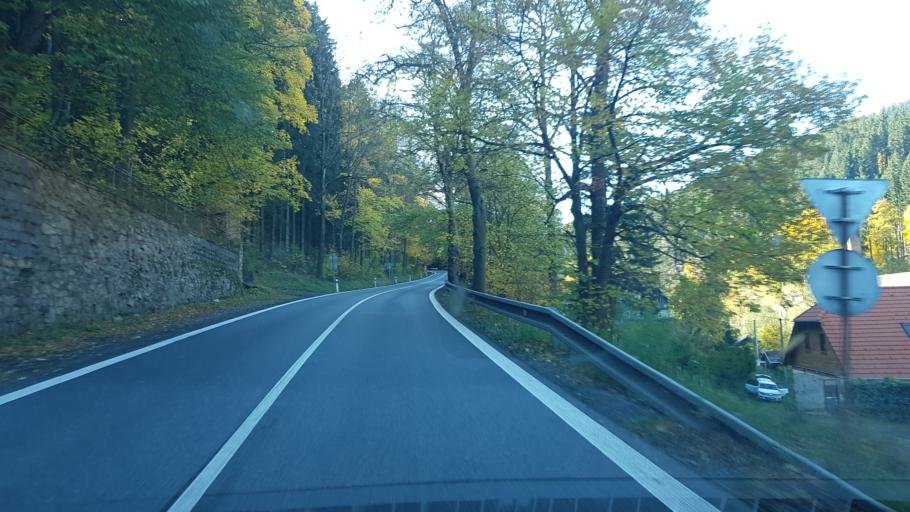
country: CZ
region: Jihocesky
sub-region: Okres Prachatice
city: Vimperk
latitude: 49.0502
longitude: 13.7687
